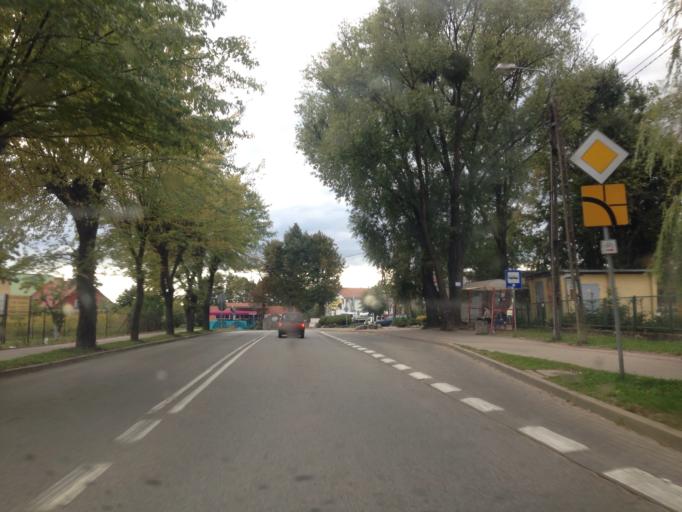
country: PL
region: Pomeranian Voivodeship
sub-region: Powiat kwidzynski
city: Prabuty
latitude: 53.7553
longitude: 19.1987
